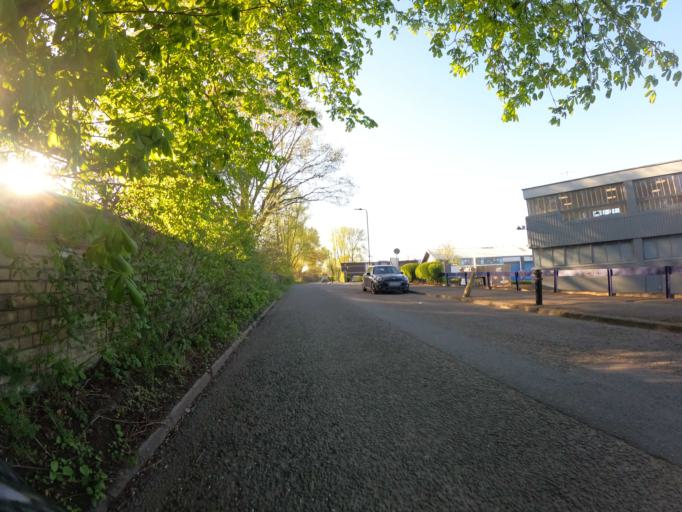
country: GB
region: England
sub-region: Greater London
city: Isleworth
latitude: 51.4989
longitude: -0.3396
